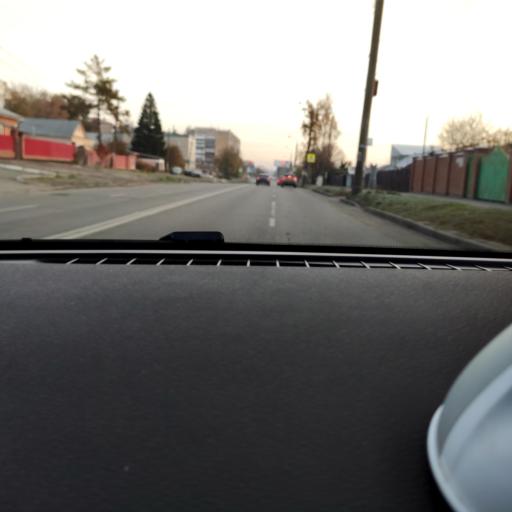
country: RU
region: Samara
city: Samara
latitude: 53.1885
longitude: 50.2081
